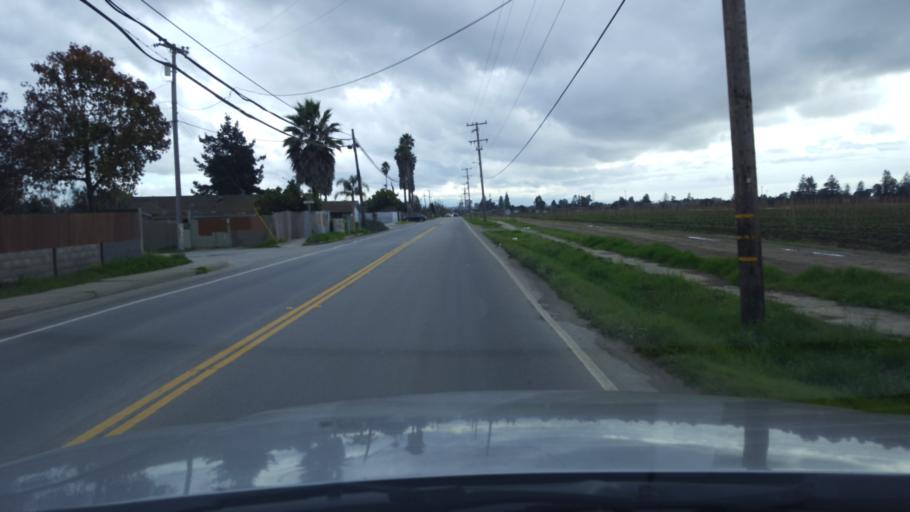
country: US
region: California
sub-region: Santa Cruz County
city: Amesti
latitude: 36.9613
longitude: -121.7650
